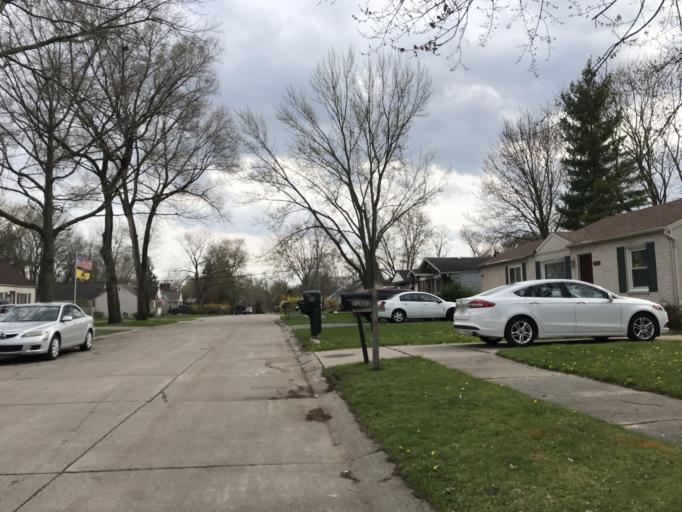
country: US
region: Michigan
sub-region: Oakland County
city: Farmington
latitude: 42.4585
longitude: -83.3404
